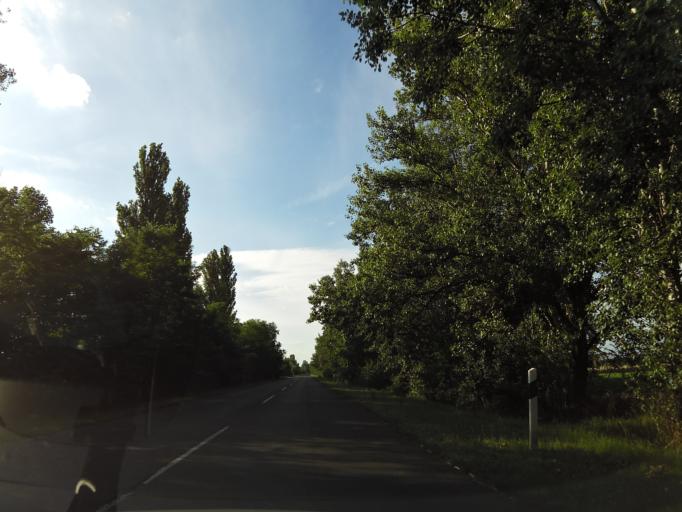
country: HU
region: Csongrad
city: Szatymaz
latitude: 46.3685
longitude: 20.0448
